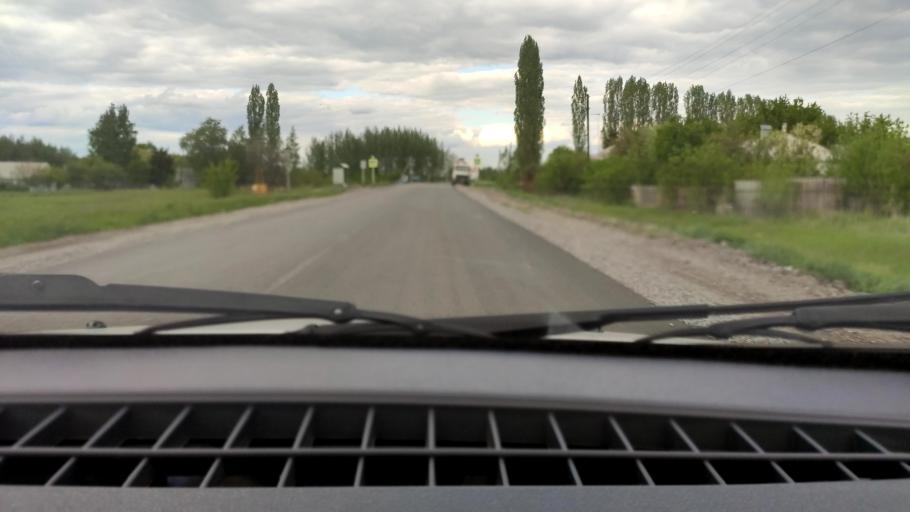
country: RU
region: Voronezj
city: Podkletnoye
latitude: 51.5899
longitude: 39.4686
